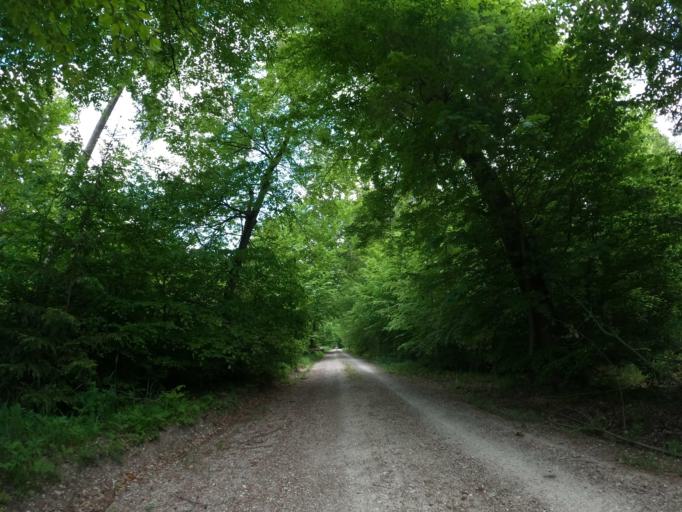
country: DE
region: Bavaria
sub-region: Upper Bavaria
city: Brunnthal
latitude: 47.9758
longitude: 11.6961
